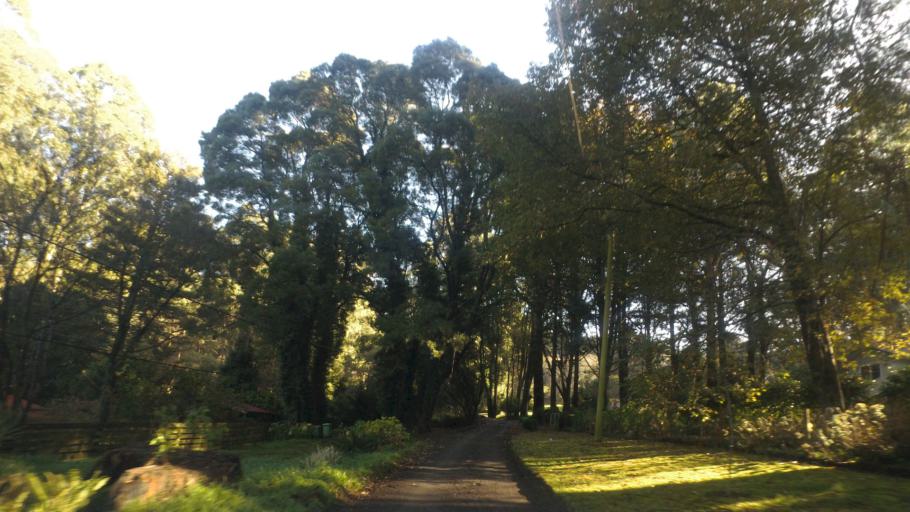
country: AU
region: Victoria
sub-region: Yarra Ranges
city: Mount Dandenong
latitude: -37.8385
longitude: 145.3511
